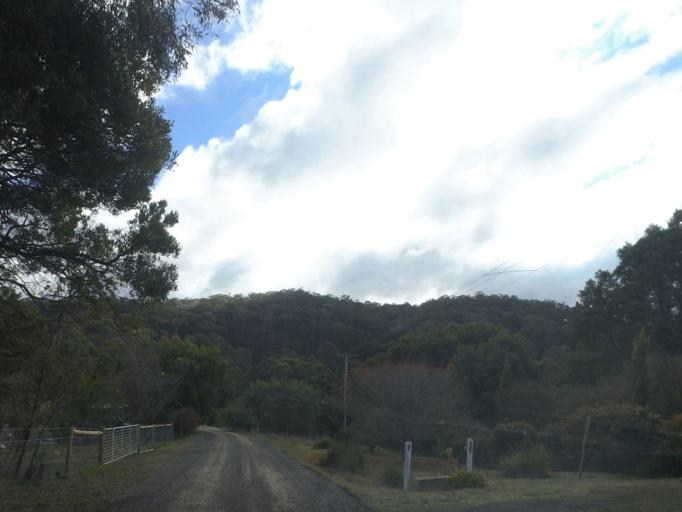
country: AU
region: Victoria
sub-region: Moorabool
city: Bacchus Marsh
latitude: -37.4670
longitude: 144.3069
